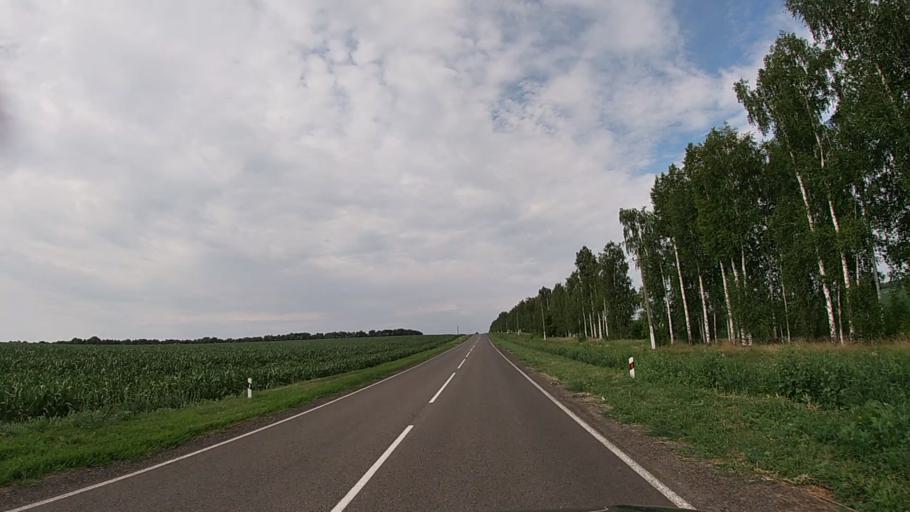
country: RU
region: Belgorod
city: Krasnaya Yaruga
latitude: 50.8229
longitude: 35.4625
